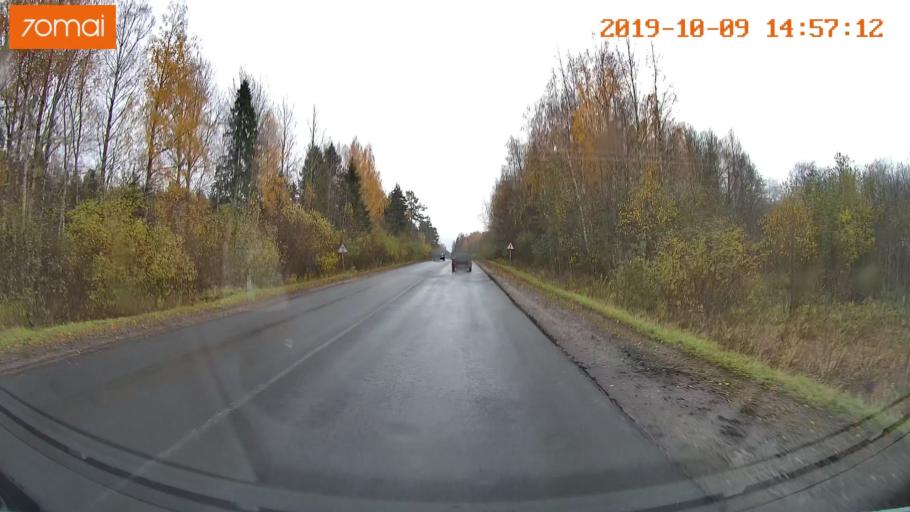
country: RU
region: Kostroma
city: Chistyye Bory
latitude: 58.3399
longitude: 41.6497
